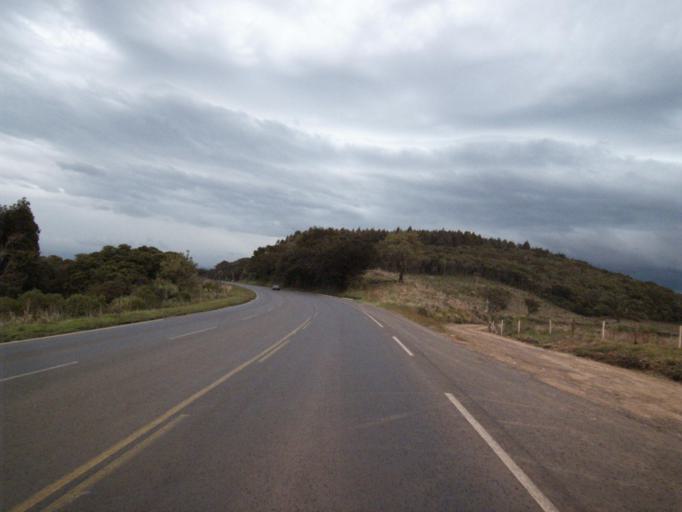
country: BR
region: Santa Catarina
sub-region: Concordia
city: Concordia
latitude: -27.0408
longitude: -51.8822
